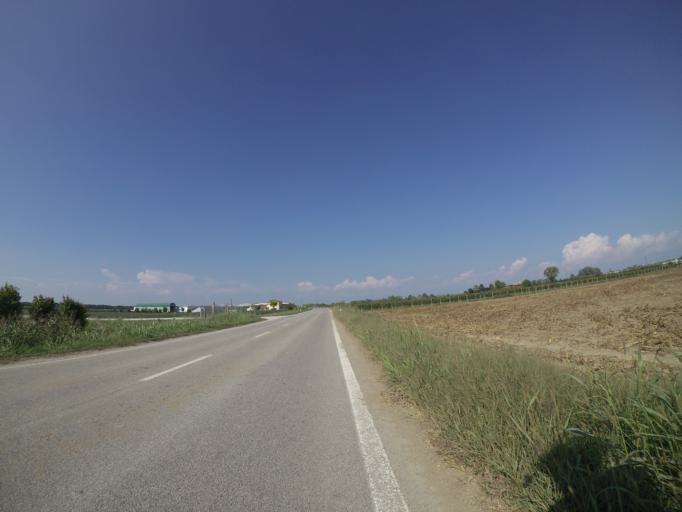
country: IT
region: Friuli Venezia Giulia
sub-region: Provincia di Udine
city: Carlino
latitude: 45.7931
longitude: 13.1656
